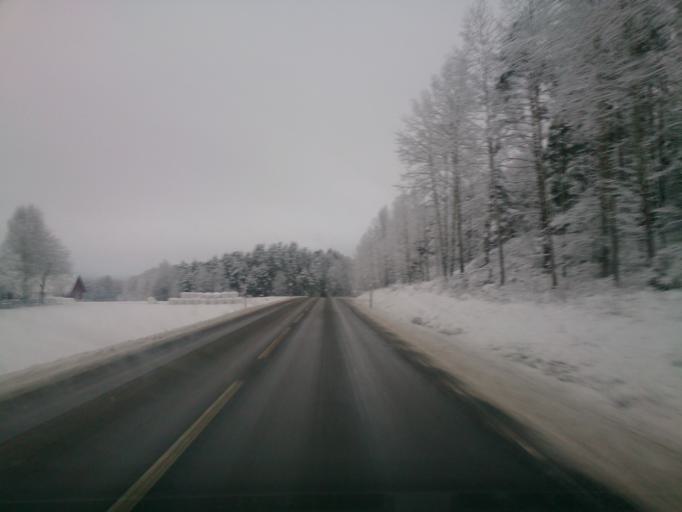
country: SE
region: OEstergoetland
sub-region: Atvidabergs Kommun
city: Atvidaberg
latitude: 58.2832
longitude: 15.9012
